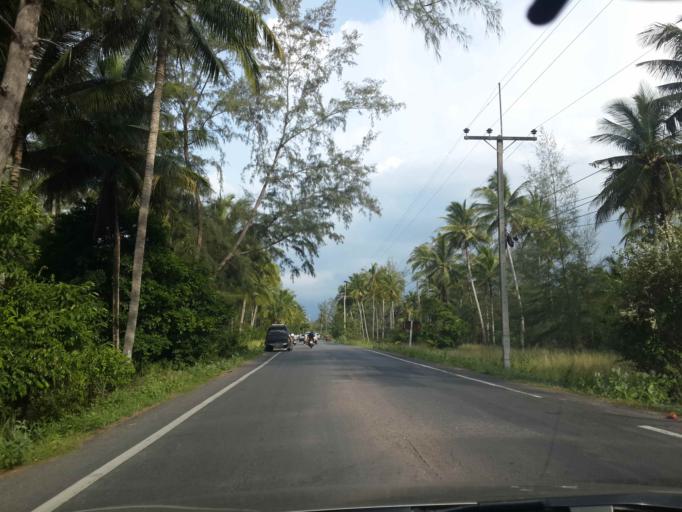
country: TH
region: Pattani
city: Yaring
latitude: 6.9032
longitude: 101.3566
